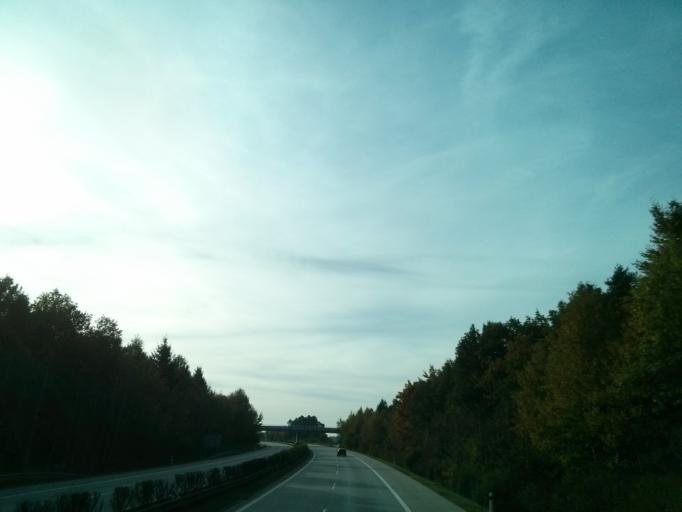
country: CZ
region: Plzensky
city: Line
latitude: 49.7103
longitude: 13.2524
